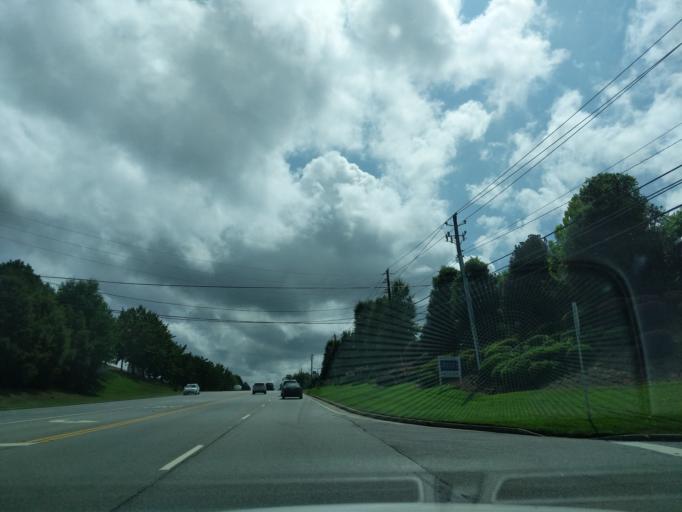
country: US
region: Georgia
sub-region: Columbia County
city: Evans
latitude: 33.5454
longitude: -82.1448
